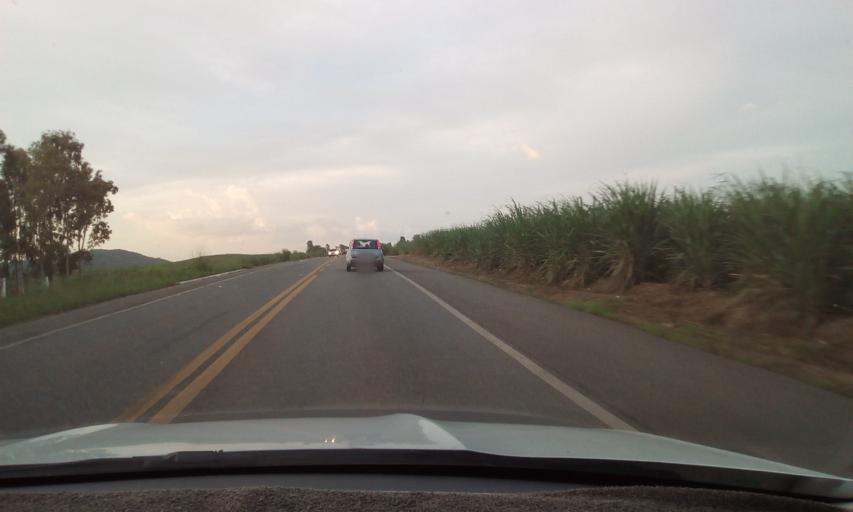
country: BR
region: Pernambuco
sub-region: Vicencia
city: Vicencia
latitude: -7.6083
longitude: -35.2399
